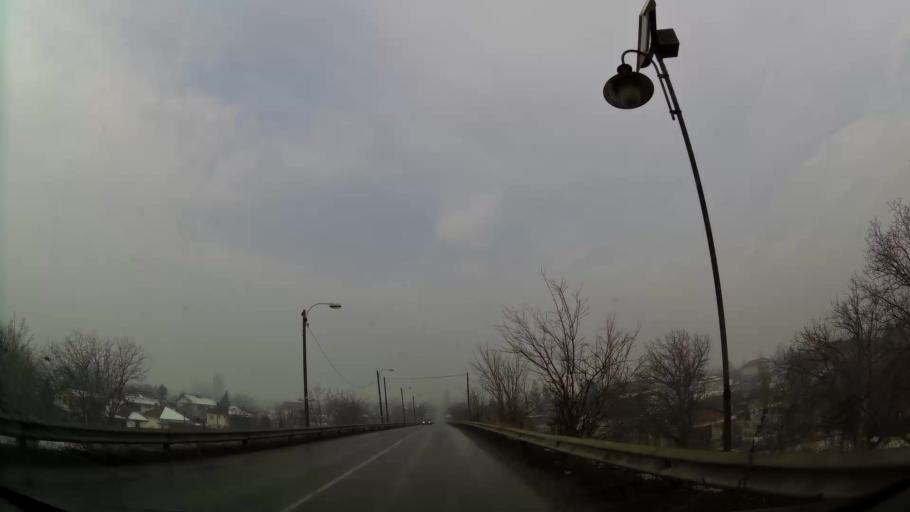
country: MK
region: Ilinden
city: Jurumleri
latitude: 41.9705
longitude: 21.5444
